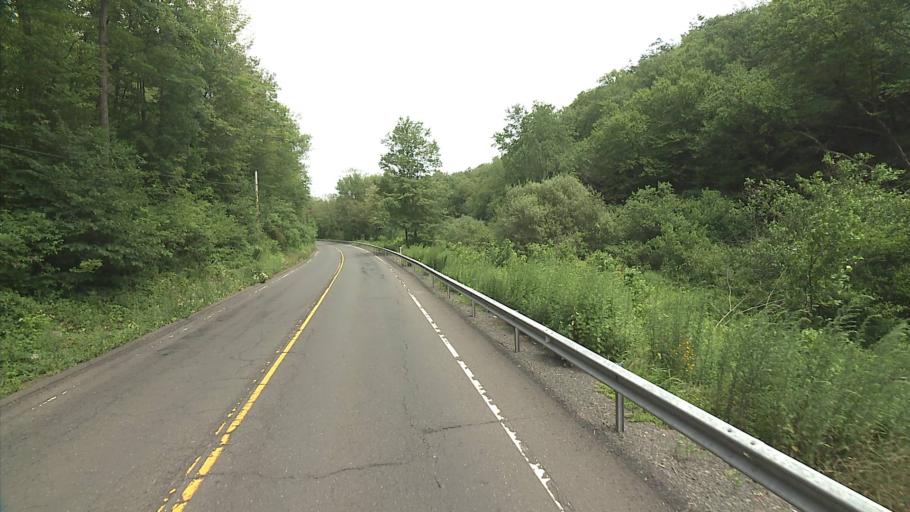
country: US
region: Connecticut
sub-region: New Haven County
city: Meriden
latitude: 41.5636
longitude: -72.8090
